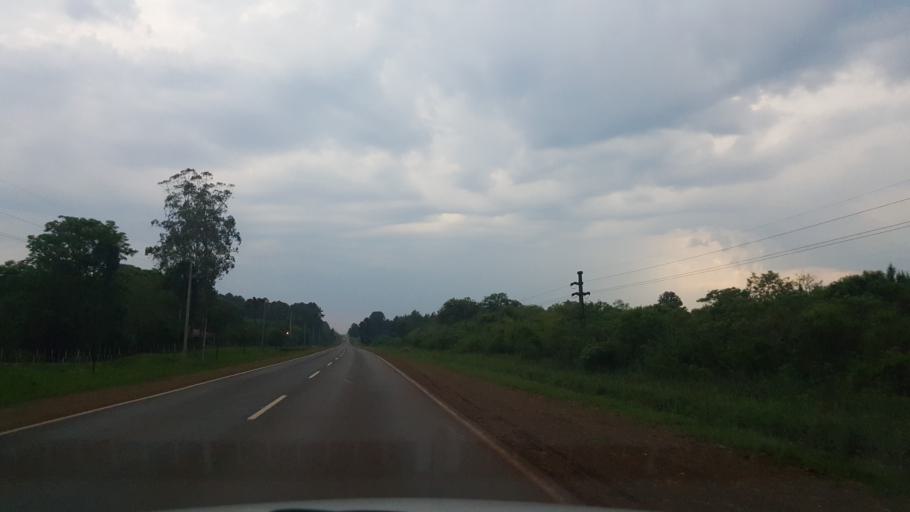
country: AR
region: Misiones
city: Jardin America
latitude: -27.0273
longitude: -55.2120
